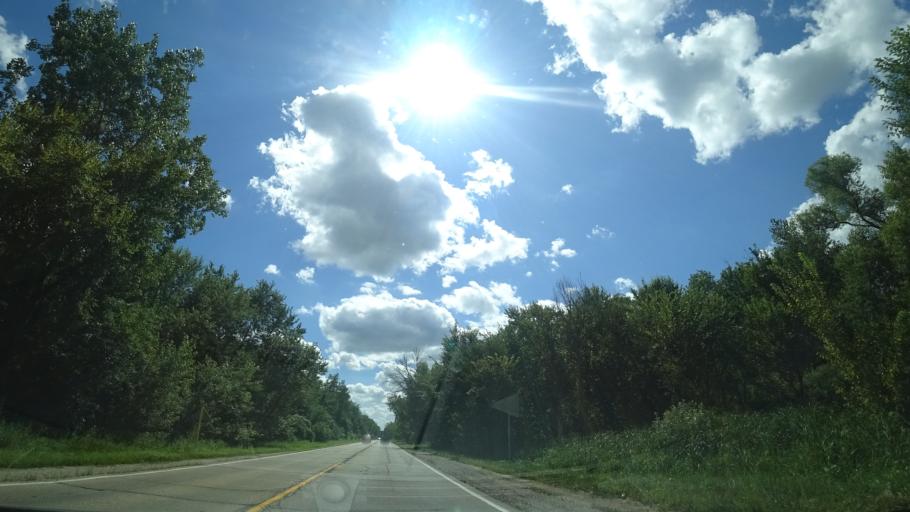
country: US
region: Illinois
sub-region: Will County
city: Mokena
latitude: 41.5552
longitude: -87.9199
